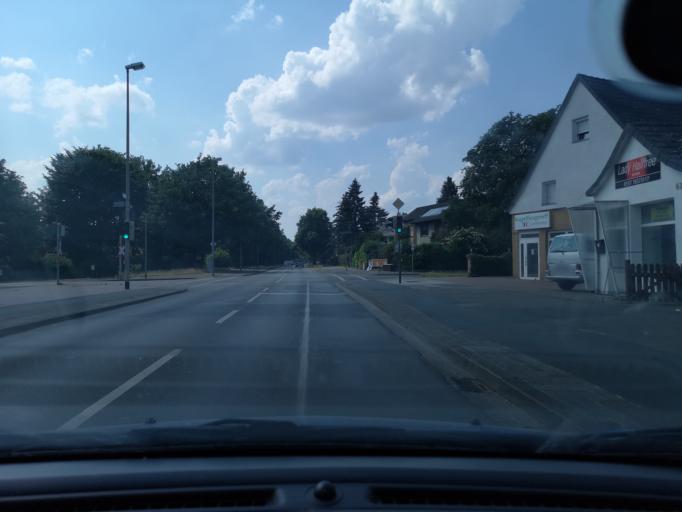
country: DE
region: Lower Saxony
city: Langenhagen
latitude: 52.4173
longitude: 9.7725
